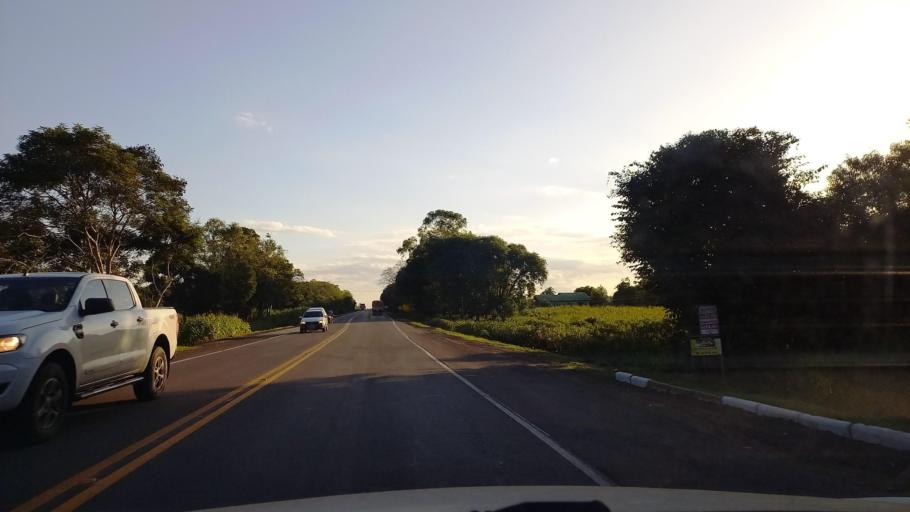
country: BR
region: Rio Grande do Sul
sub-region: Venancio Aires
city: Venancio Aires
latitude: -29.6579
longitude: -52.2356
